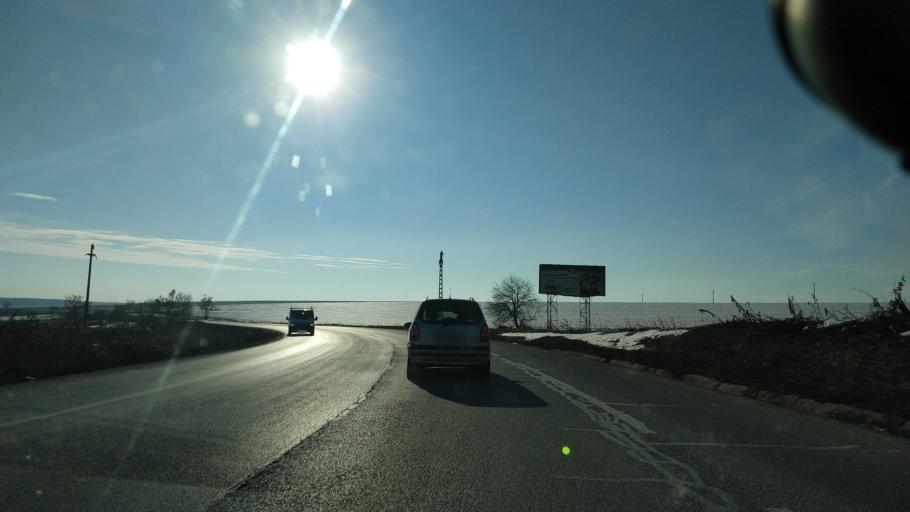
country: RO
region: Iasi
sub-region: Comuna Strunga
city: Strunga
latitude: 47.1571
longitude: 26.9466
